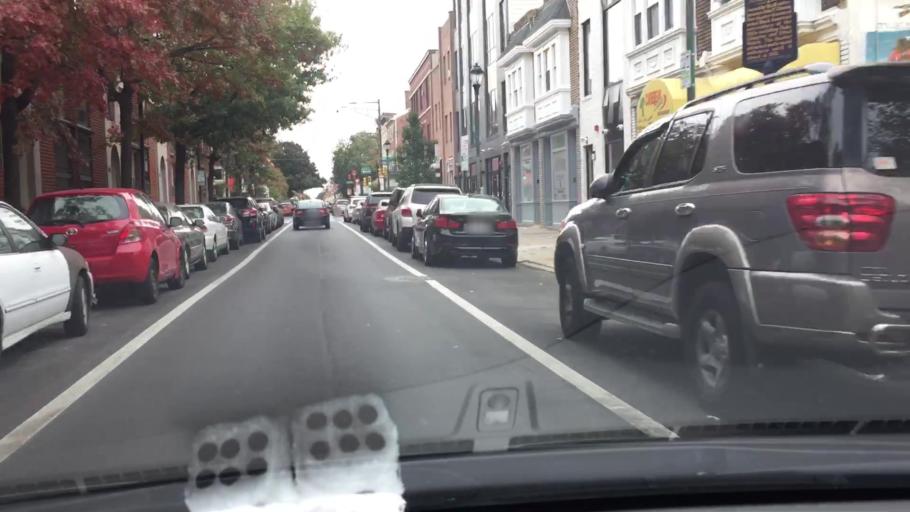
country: US
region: Pennsylvania
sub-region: Philadelphia County
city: Philadelphia
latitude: 39.9431
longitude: -75.1612
